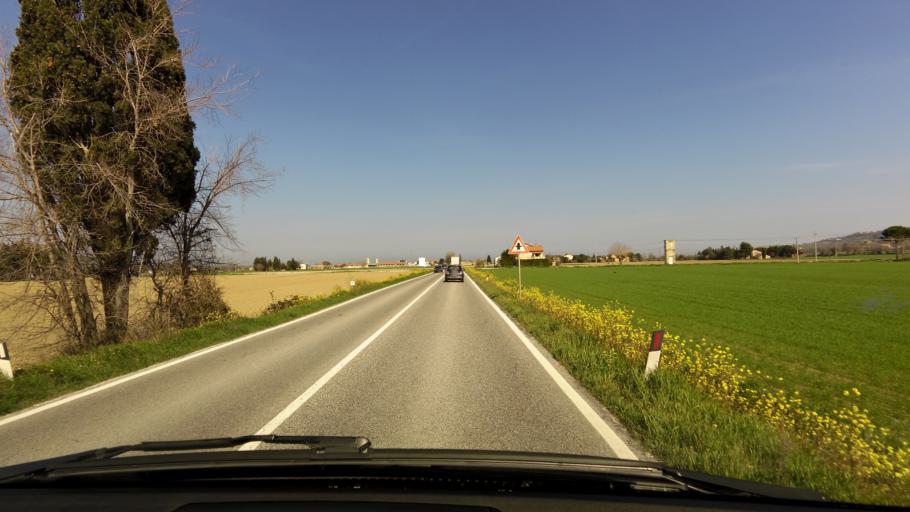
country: IT
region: The Marches
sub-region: Provincia di Macerata
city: Potenza Picena
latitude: 43.3868
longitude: 13.6247
